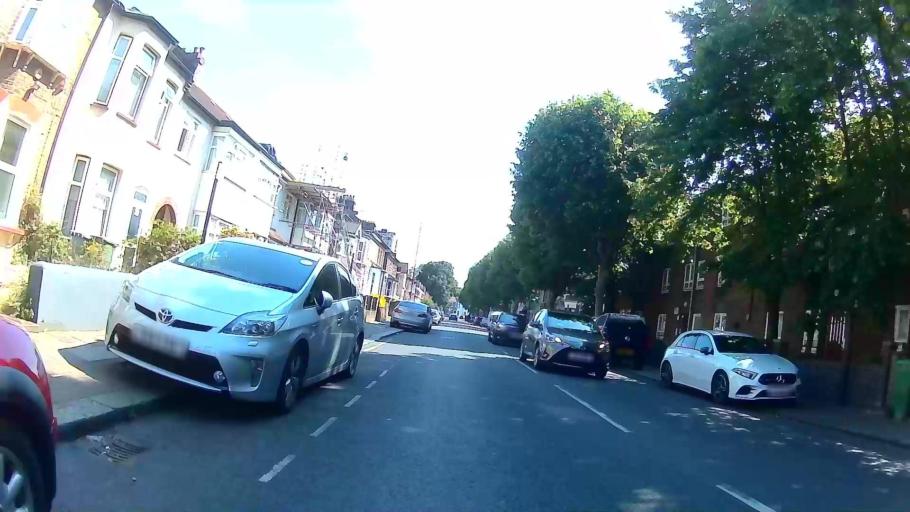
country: GB
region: England
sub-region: Greater London
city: East Ham
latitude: 51.5348
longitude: 0.0223
